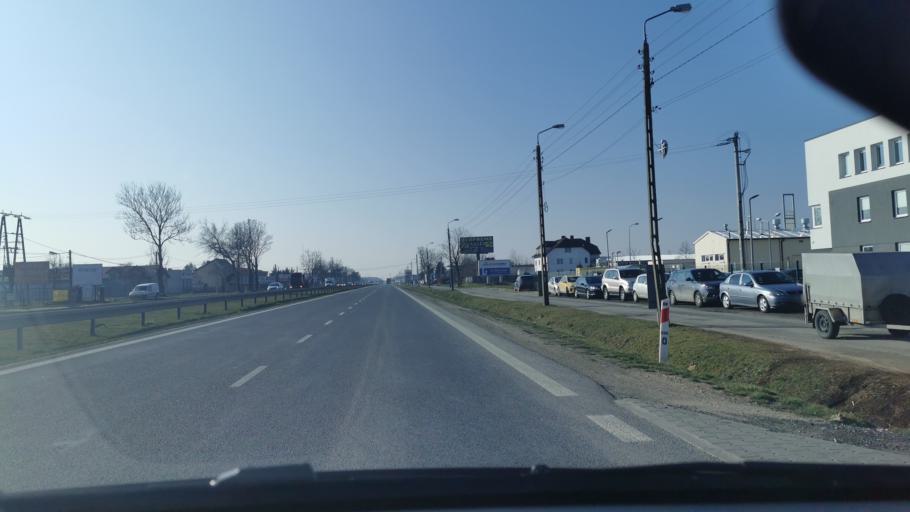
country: PL
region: Masovian Voivodeship
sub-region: Powiat pruszkowski
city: Nowe Grocholice
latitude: 52.1216
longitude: 20.8937
